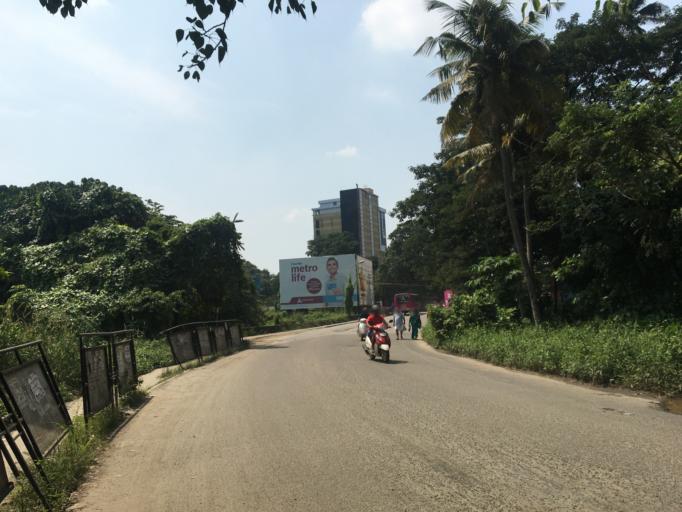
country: IN
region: Kerala
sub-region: Ernakulam
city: Cochin
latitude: 9.9667
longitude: 76.3202
